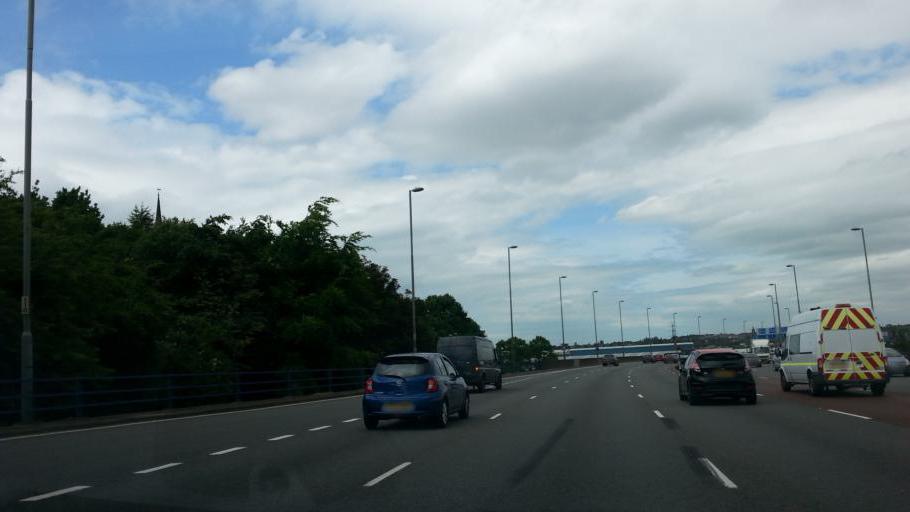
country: GB
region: England
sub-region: City and Borough of Birmingham
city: Birmingham
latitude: 52.5054
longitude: -1.8802
